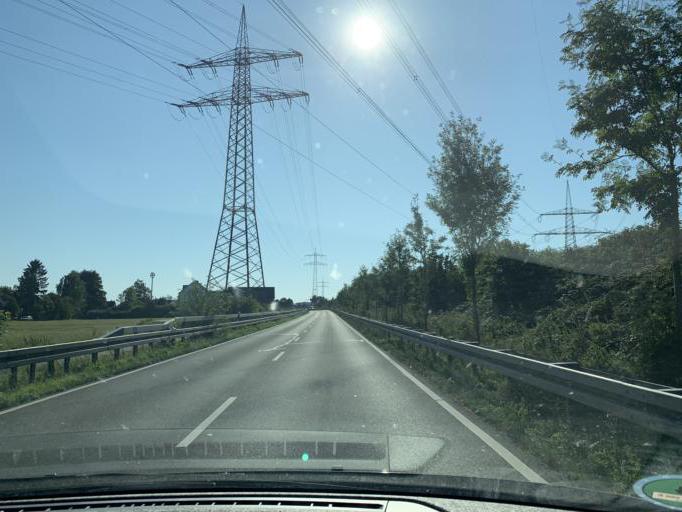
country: DE
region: North Rhine-Westphalia
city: Schwerte
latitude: 51.4586
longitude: 7.5680
